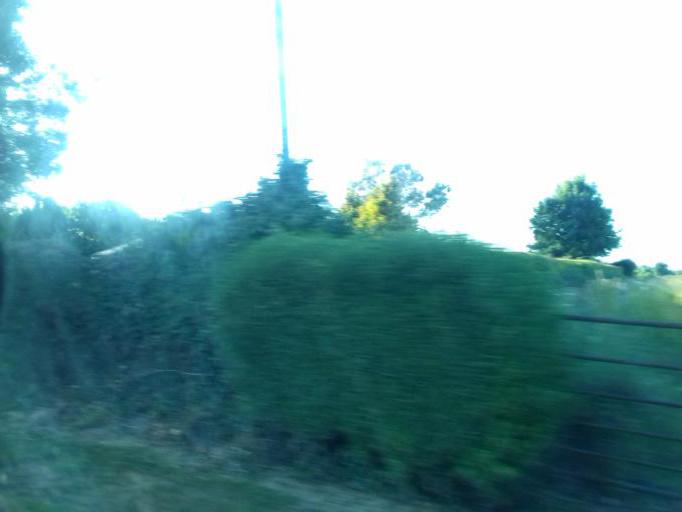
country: IE
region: Leinster
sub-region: Dublin City
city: Finglas
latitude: 53.4310
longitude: -6.3204
